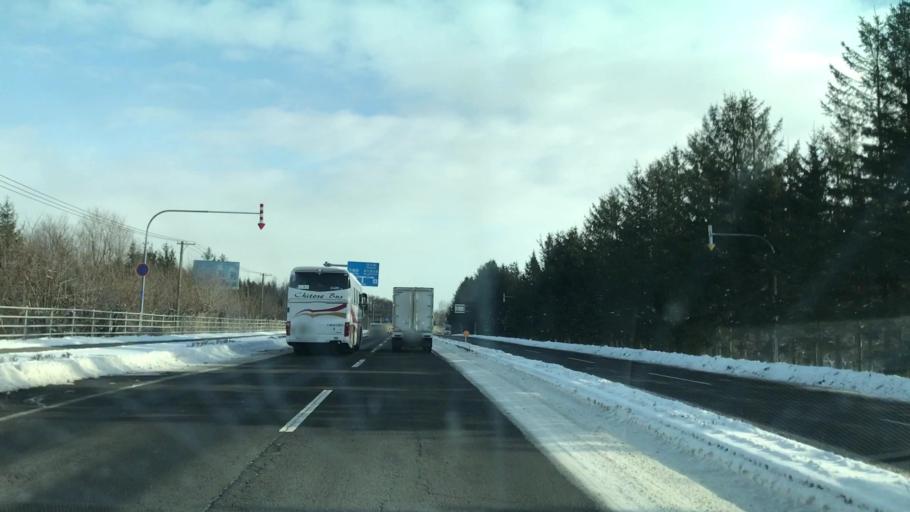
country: JP
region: Hokkaido
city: Chitose
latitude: 42.8176
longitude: 141.6574
